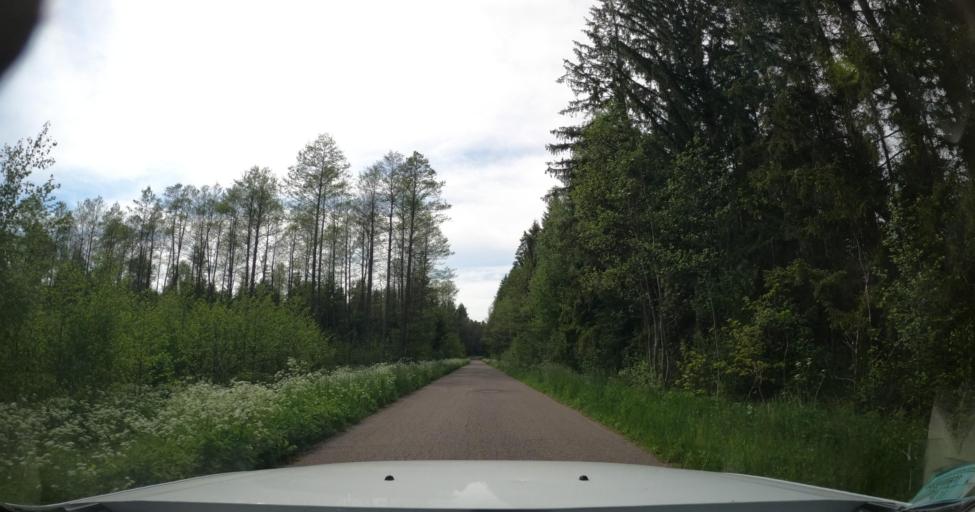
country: PL
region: Warmian-Masurian Voivodeship
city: Dobre Miasto
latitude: 54.0956
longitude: 20.3944
